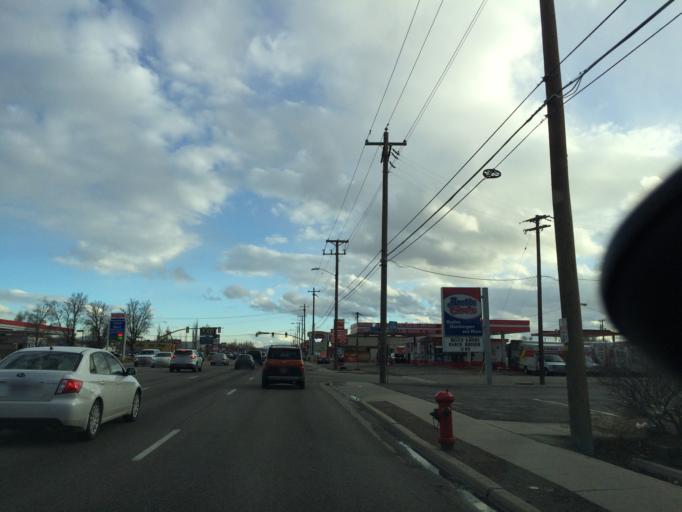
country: US
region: Utah
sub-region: Salt Lake County
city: Taylorsville
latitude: 40.6655
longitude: -111.9390
